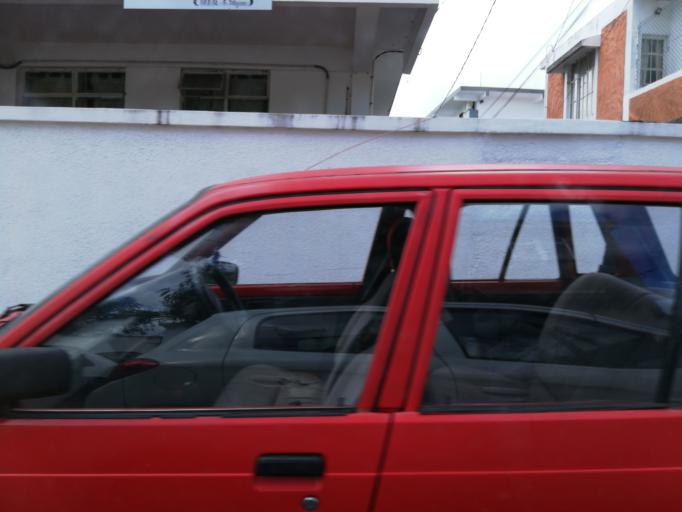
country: MU
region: Port Louis
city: Port Louis
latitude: -20.1619
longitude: 57.4818
